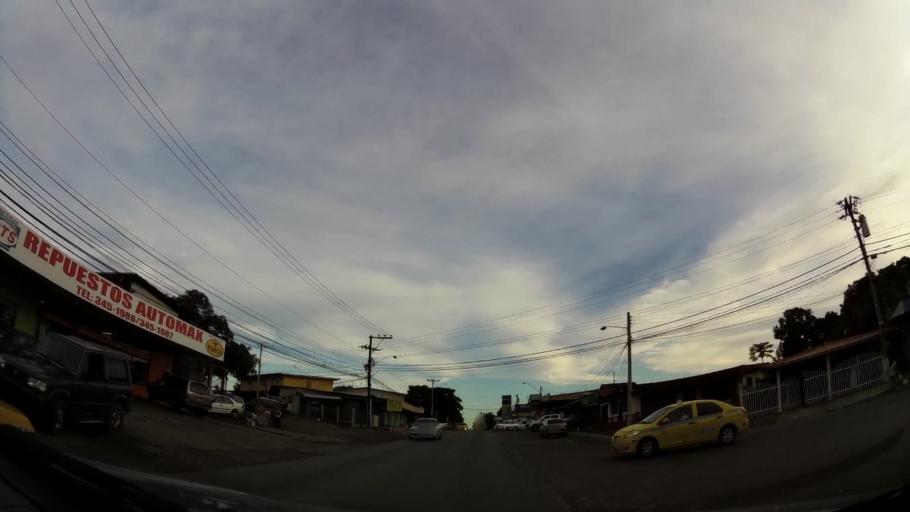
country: PA
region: Panama
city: La Chorrera
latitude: 8.8763
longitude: -79.7792
